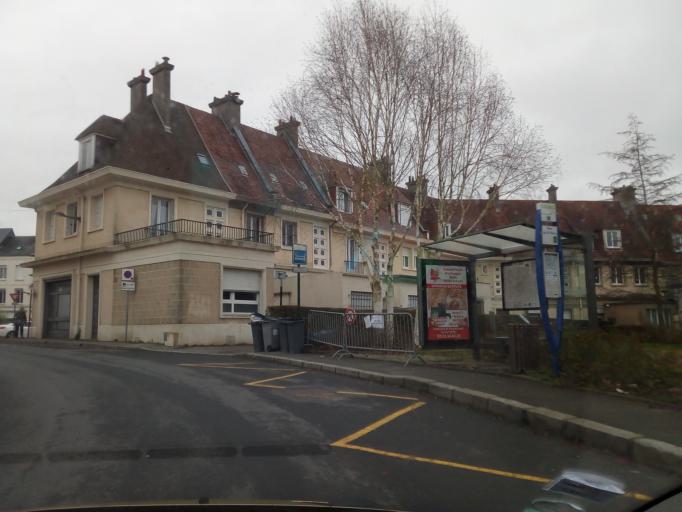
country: FR
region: Haute-Normandie
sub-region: Departement de la Seine-Maritime
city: Yvetot
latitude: 49.6163
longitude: 0.7549
